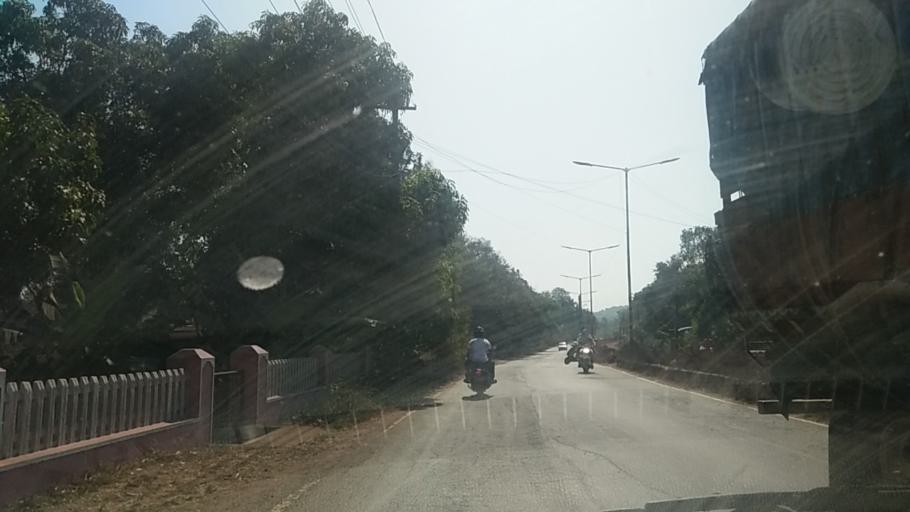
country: IN
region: Goa
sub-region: South Goa
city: Raia
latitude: 15.3170
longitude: 73.9832
